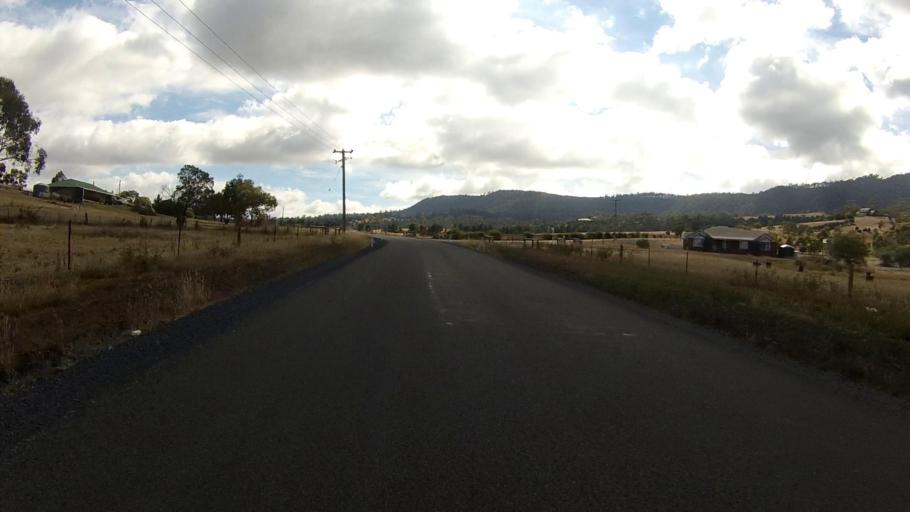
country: AU
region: Tasmania
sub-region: Brighton
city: Old Beach
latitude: -42.7669
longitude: 147.2984
